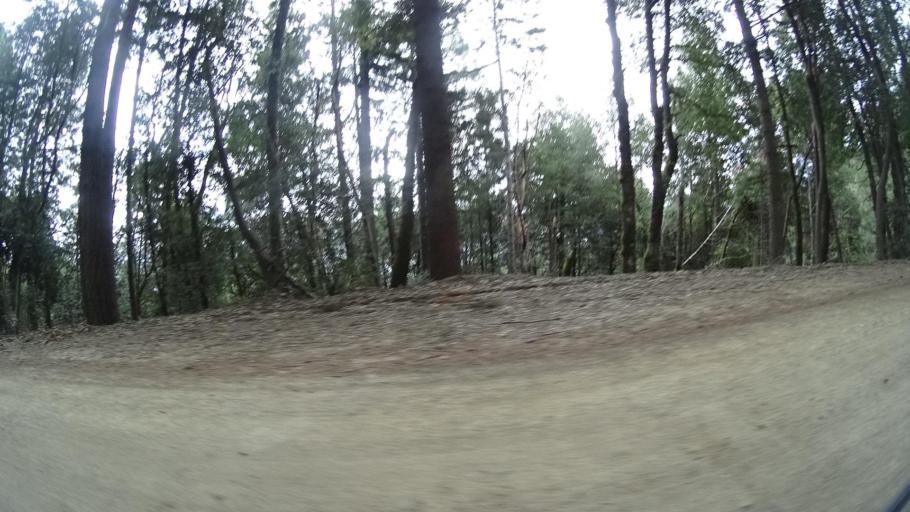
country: US
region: California
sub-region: Humboldt County
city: Redway
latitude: 40.2625
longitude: -123.7685
